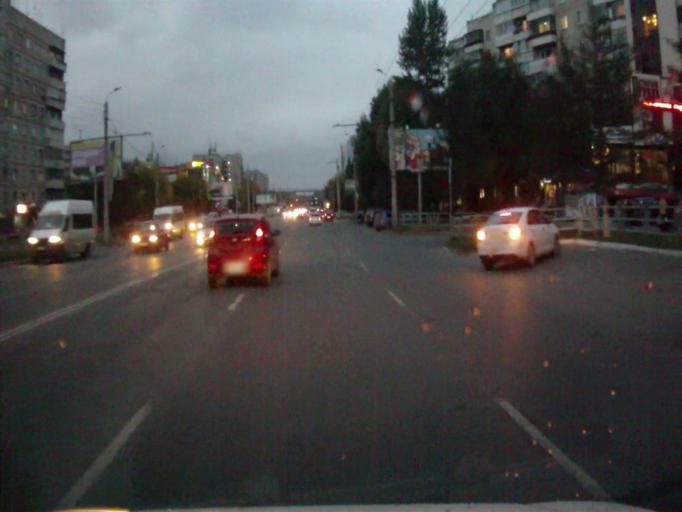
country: RU
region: Chelyabinsk
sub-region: Gorod Chelyabinsk
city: Chelyabinsk
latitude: 55.1827
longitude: 61.3326
